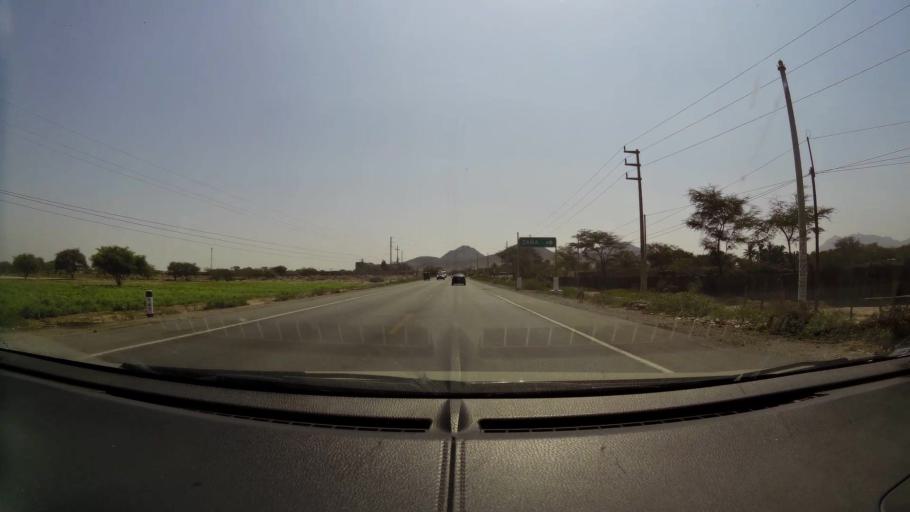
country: PE
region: Lambayeque
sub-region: Provincia de Chiclayo
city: Mocupe
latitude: -6.9809
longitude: -79.6411
